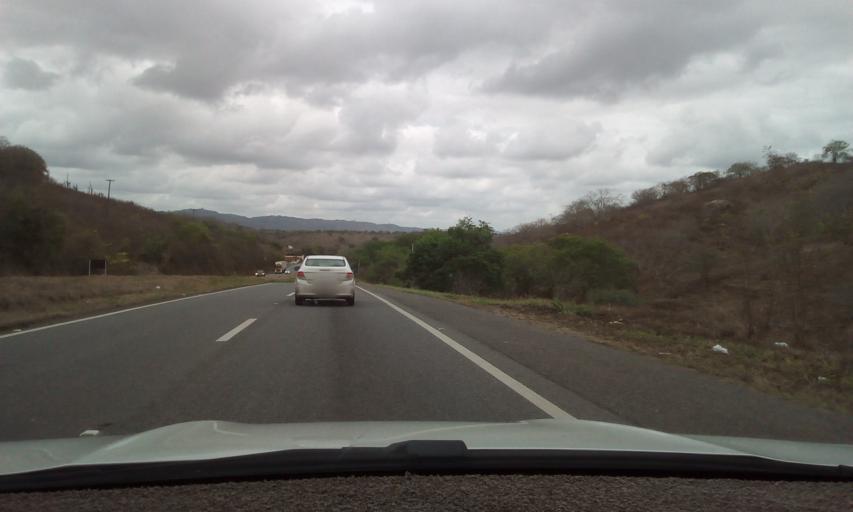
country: BR
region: Paraiba
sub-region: Massaranduba
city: Massaranduba
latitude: -7.2746
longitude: -35.7545
